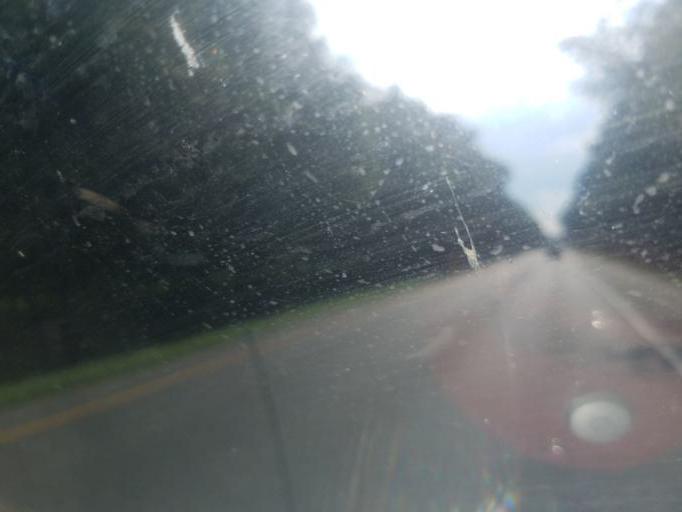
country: US
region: Maryland
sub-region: Wicomico County
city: Pittsville
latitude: 38.3850
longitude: -75.3077
